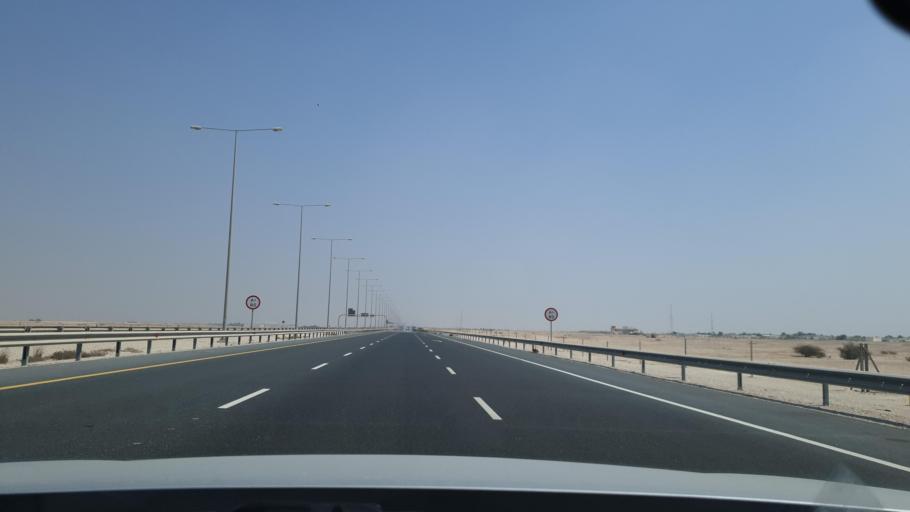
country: QA
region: Baladiyat az Za`ayin
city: Az Za`ayin
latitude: 25.6184
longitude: 51.3804
